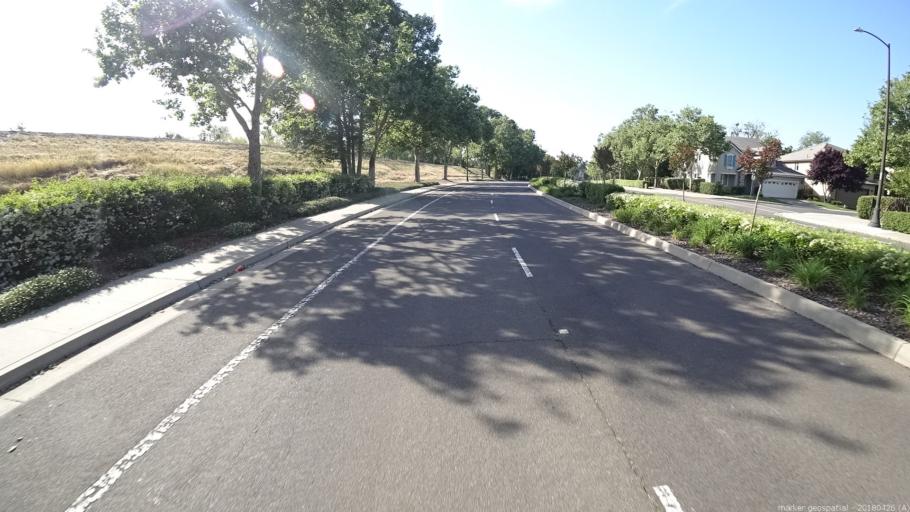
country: US
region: California
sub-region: Sacramento County
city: Sacramento
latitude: 38.5940
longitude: -121.5125
